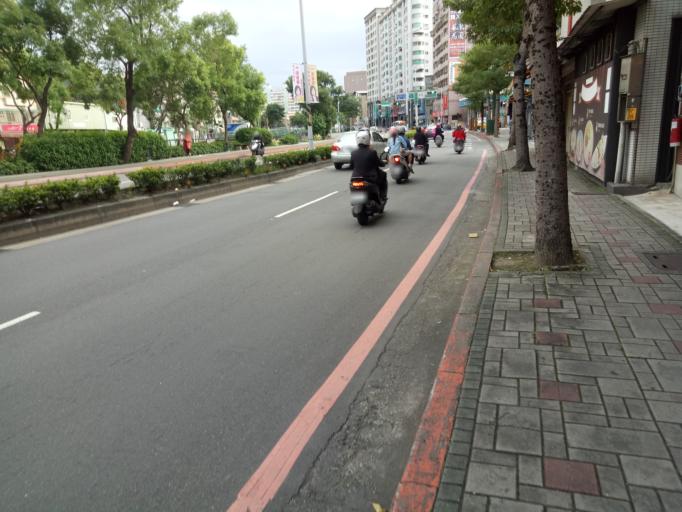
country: TW
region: Taipei
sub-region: Taipei
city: Banqiao
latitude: 25.0490
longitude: 121.4526
